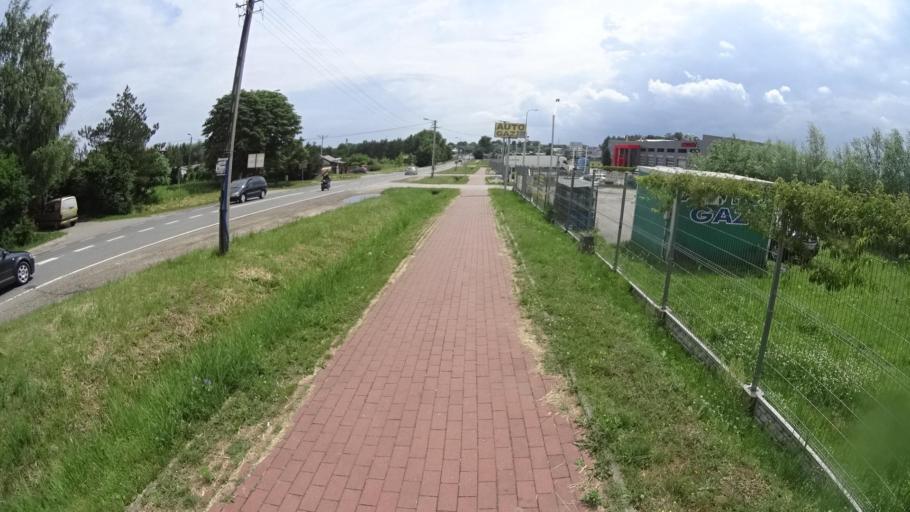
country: PL
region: Masovian Voivodeship
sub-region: Powiat grojecki
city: Grojec
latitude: 51.8778
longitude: 20.8640
